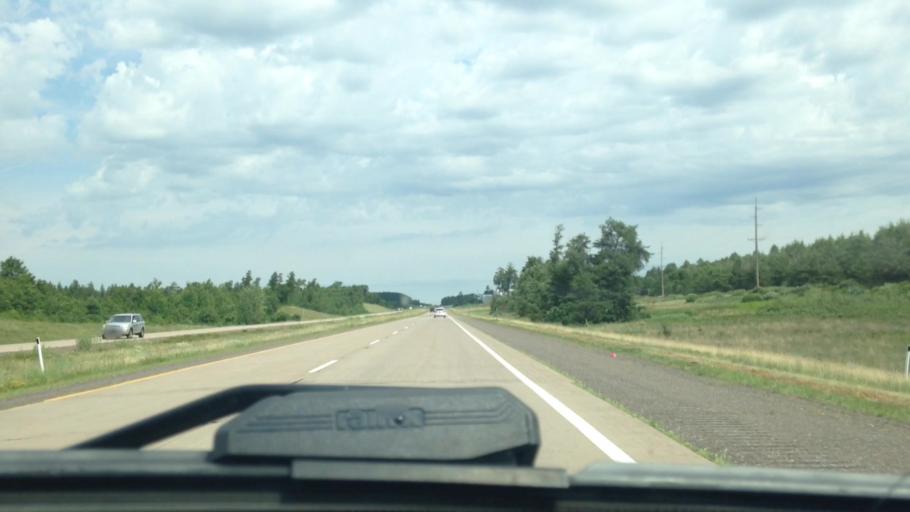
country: US
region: Wisconsin
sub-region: Douglas County
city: Lake Nebagamon
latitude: 46.1908
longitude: -91.7990
